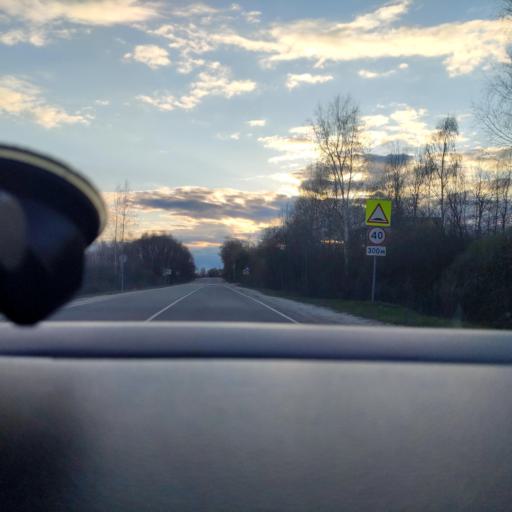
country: RU
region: Moskovskaya
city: Krasnyy Tkach
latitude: 55.4286
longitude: 39.2084
